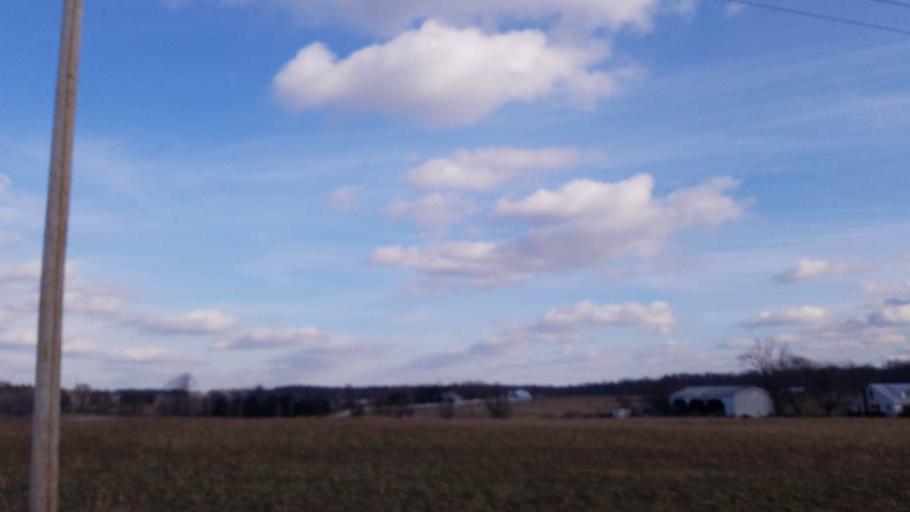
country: US
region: Ohio
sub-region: Crawford County
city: Galion
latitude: 40.6671
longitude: -82.7185
